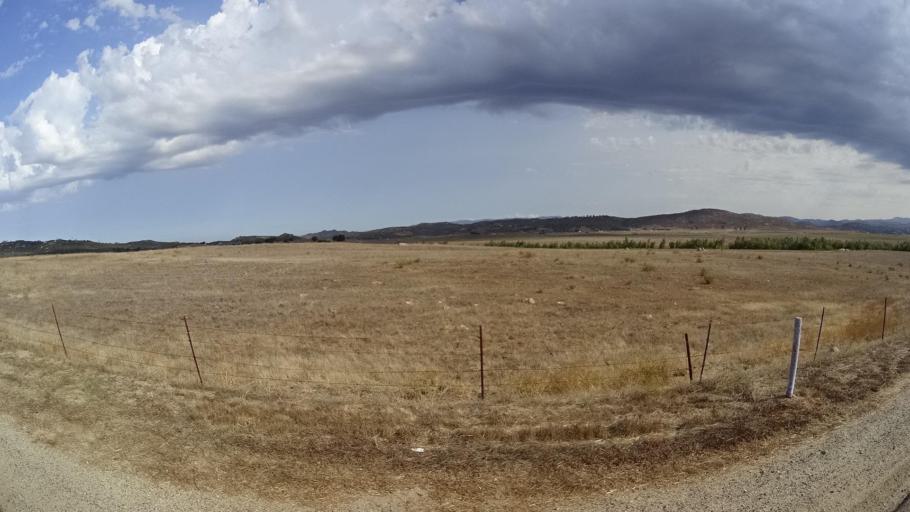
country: US
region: California
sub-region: San Diego County
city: San Pasqual
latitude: 33.0332
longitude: -116.9417
